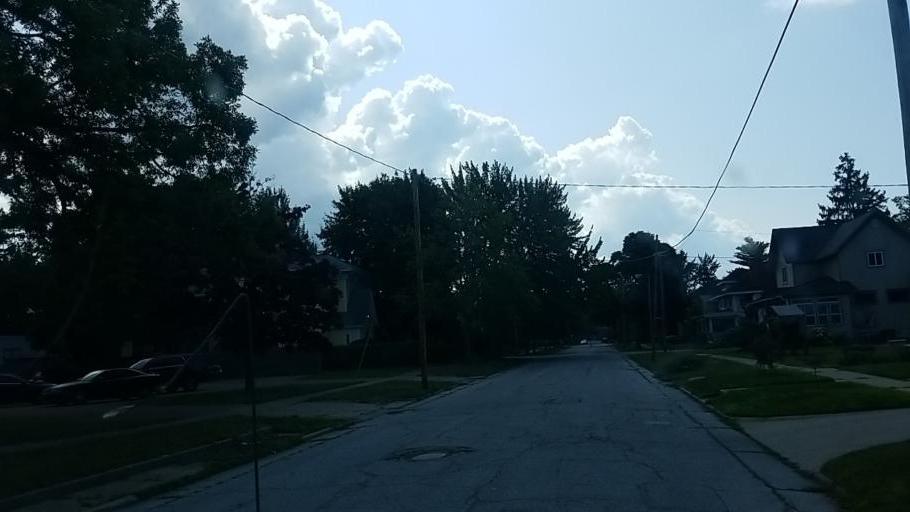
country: US
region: Michigan
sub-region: Muskegon County
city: Muskegon
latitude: 43.2303
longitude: -86.2430
